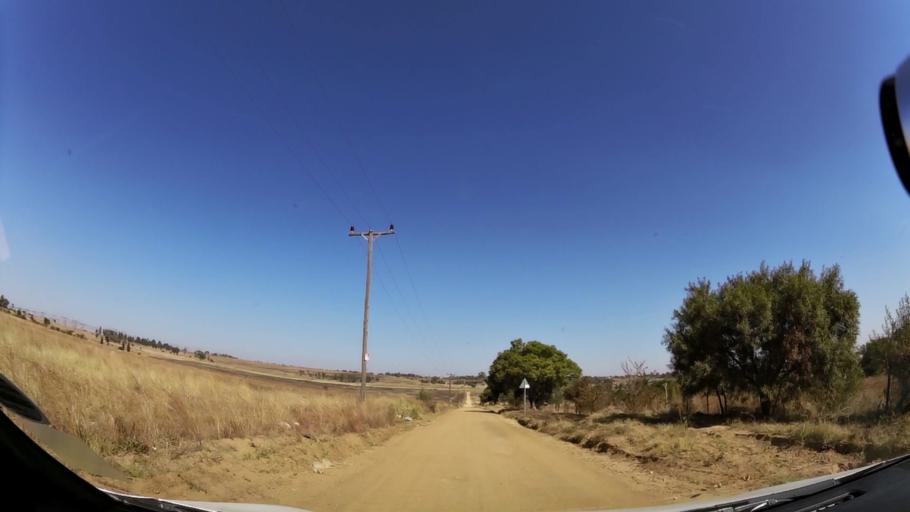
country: ZA
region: Gauteng
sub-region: City of Johannesburg Metropolitan Municipality
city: Diepsloot
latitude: -25.9020
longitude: 28.0734
